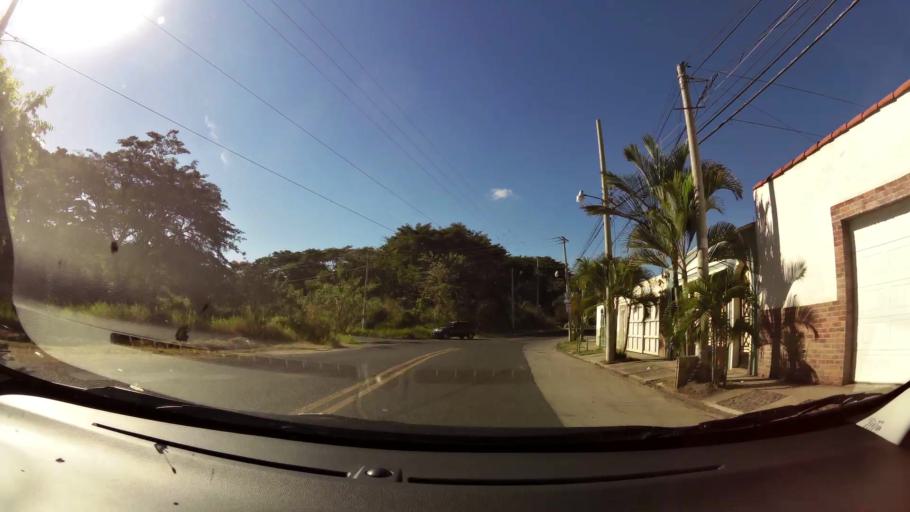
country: SV
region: Santa Ana
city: Santa Ana
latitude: 13.9629
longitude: -89.5755
